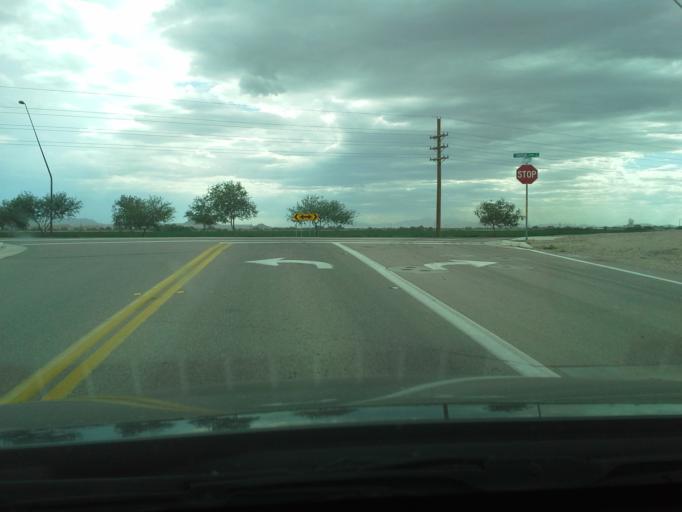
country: US
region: Arizona
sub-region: Pima County
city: Marana
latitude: 32.4249
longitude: -111.1716
